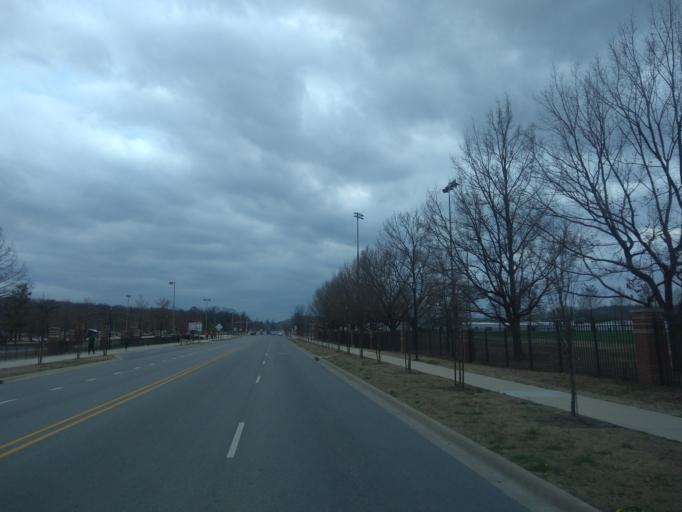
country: US
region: Arkansas
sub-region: Washington County
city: Fayetteville
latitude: 36.0595
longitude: -94.1804
